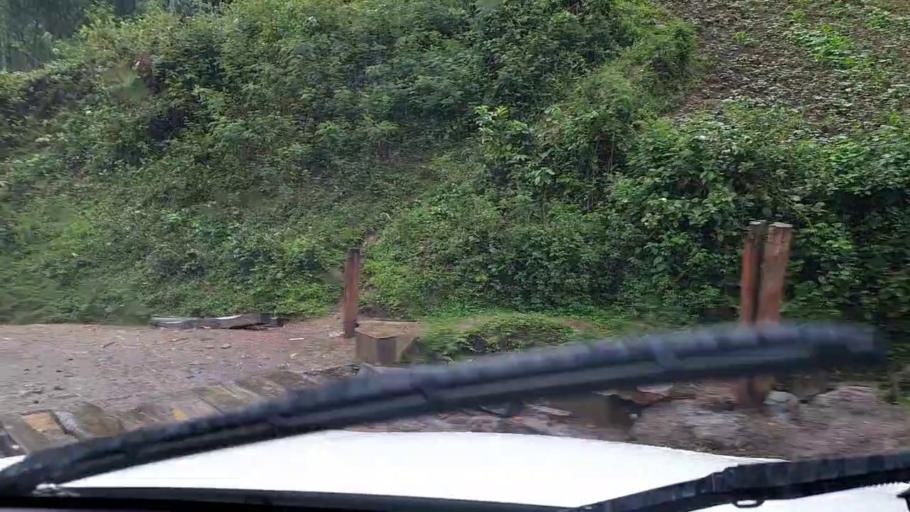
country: RW
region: Western Province
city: Cyangugu
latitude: -2.5328
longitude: 29.0432
